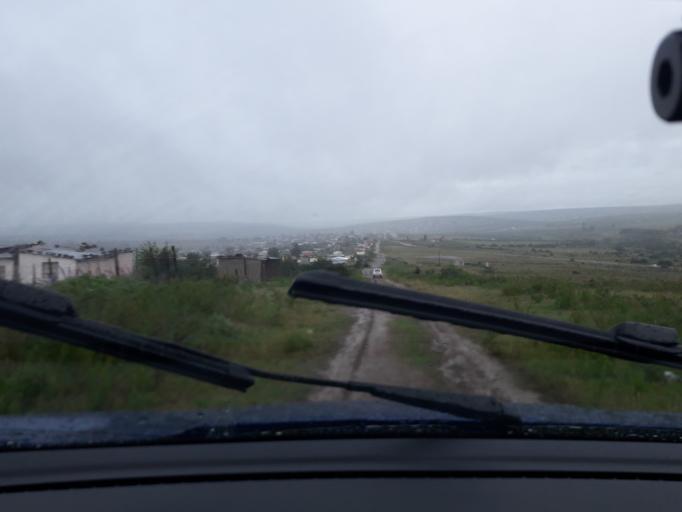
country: ZA
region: Eastern Cape
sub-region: Buffalo City Metropolitan Municipality
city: Bhisho
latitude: -32.8047
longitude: 27.3632
